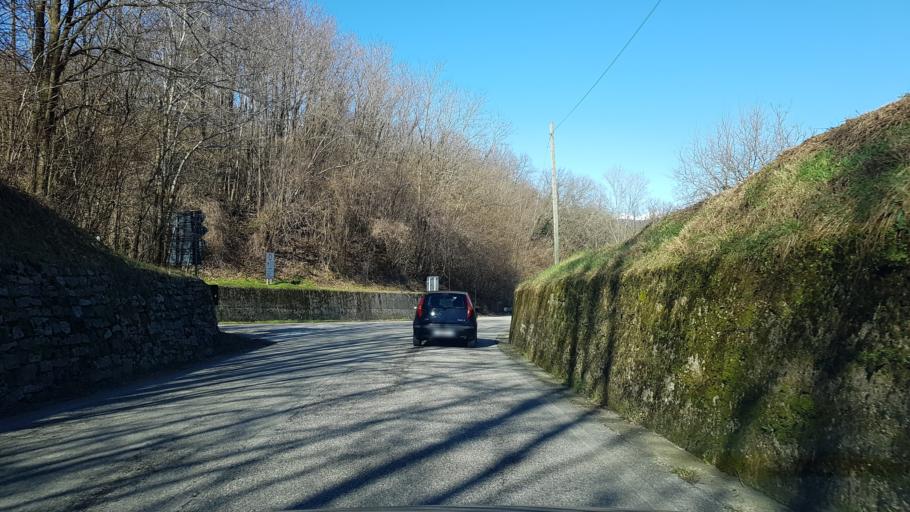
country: IT
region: Friuli Venezia Giulia
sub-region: Provincia di Udine
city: Attimis
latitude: 46.1642
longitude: 13.2962
